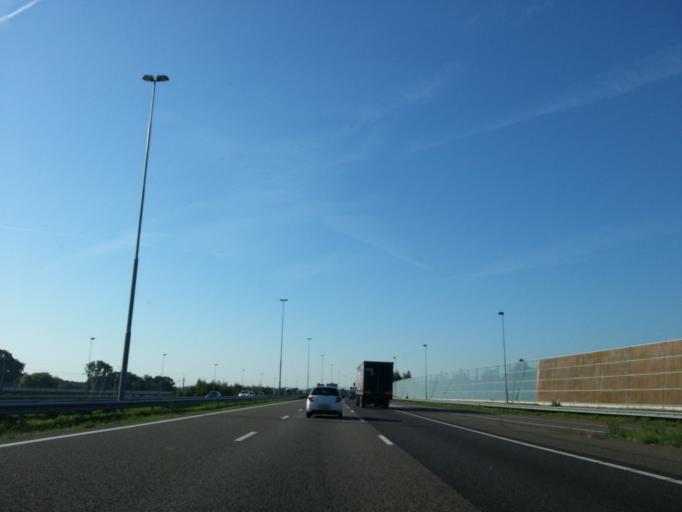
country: NL
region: North Brabant
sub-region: Gemeente Breda
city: Breda
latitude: 51.5610
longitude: 4.7343
